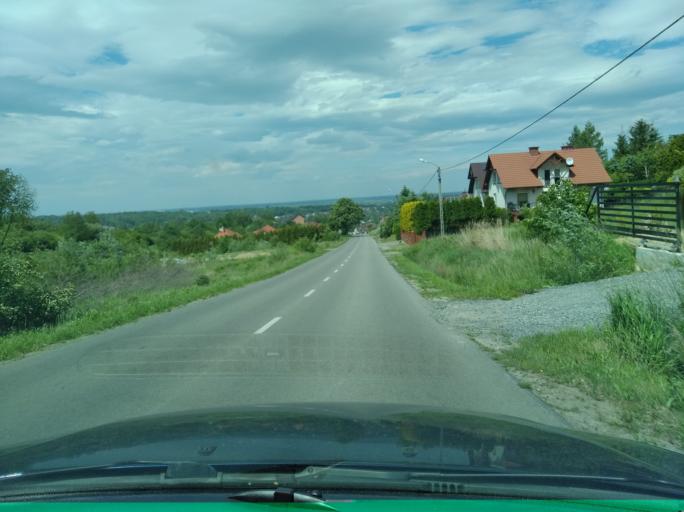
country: PL
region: Subcarpathian Voivodeship
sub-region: Powiat ropczycko-sedziszowski
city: Ropczyce
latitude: 50.0416
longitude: 21.6196
